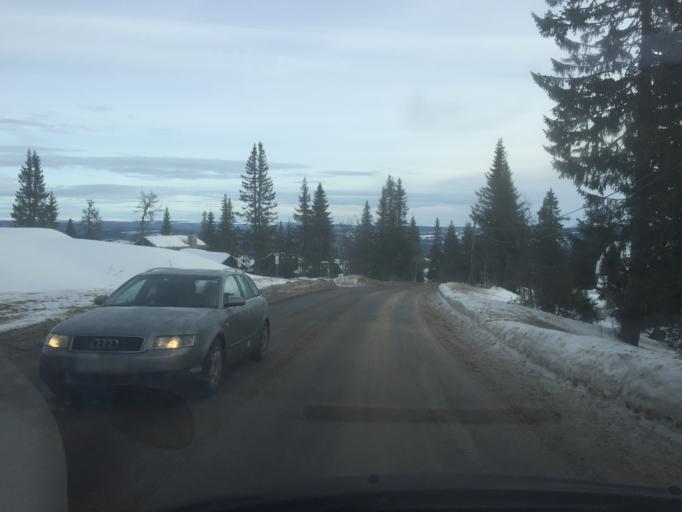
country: NO
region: Hedmark
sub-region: Trysil
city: Innbygda
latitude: 61.3292
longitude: 12.1559
